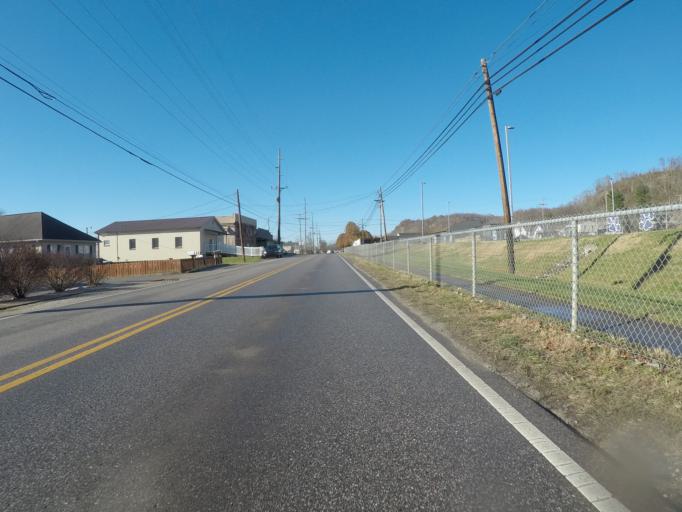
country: US
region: West Virginia
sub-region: Cabell County
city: Huntington
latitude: 38.4264
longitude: -82.4646
